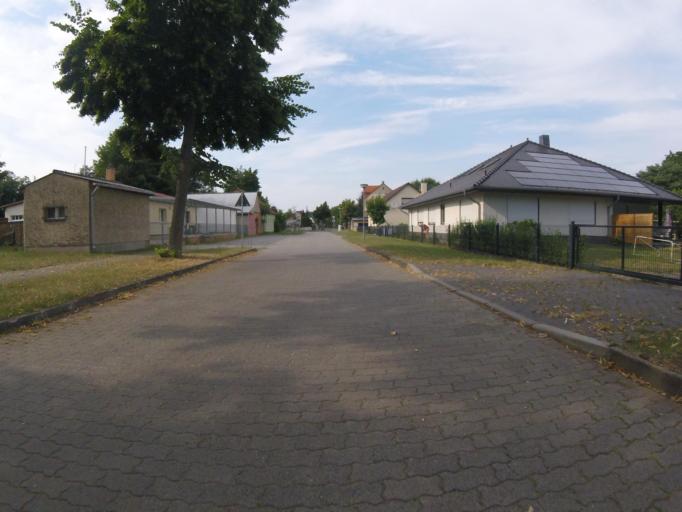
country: DE
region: Brandenburg
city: Munchehofe
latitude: 52.2558
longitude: 13.7997
